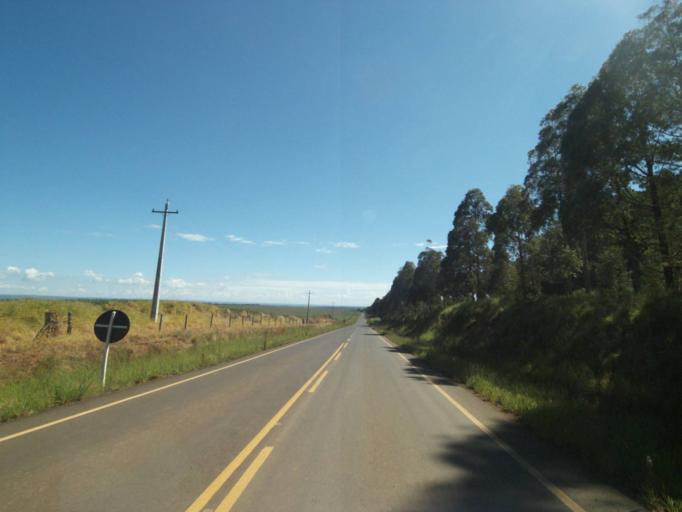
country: BR
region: Parana
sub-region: Pinhao
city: Pinhao
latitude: -25.8319
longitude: -52.0207
